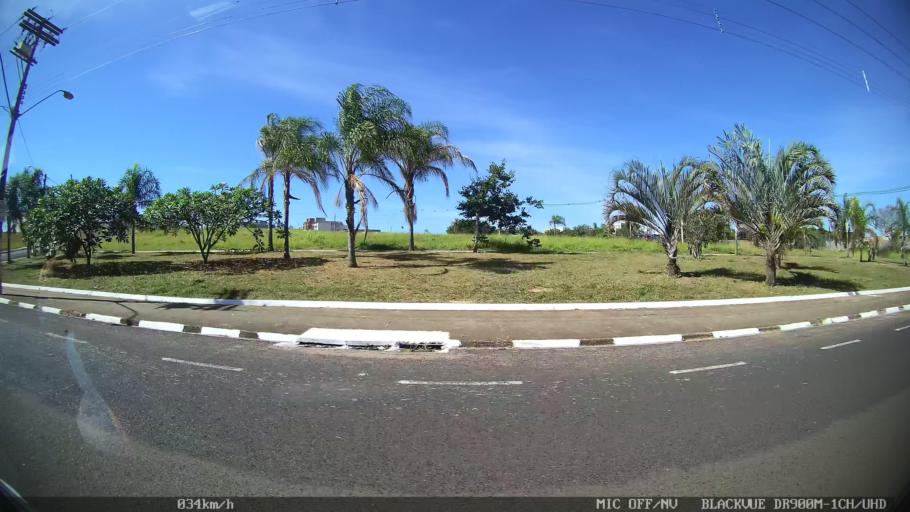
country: BR
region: Sao Paulo
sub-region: Franca
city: Franca
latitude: -20.5358
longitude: -47.3777
